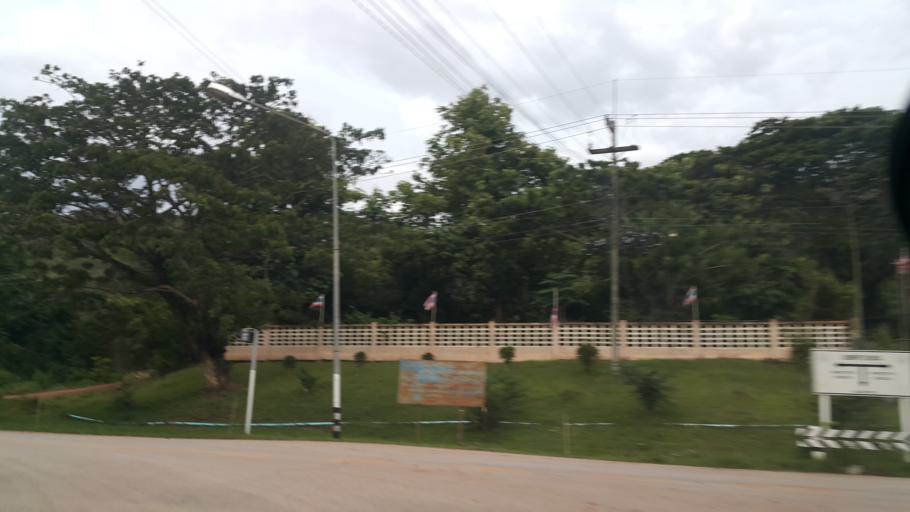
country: TH
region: Loei
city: Na Haeo
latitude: 17.4944
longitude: 101.1846
